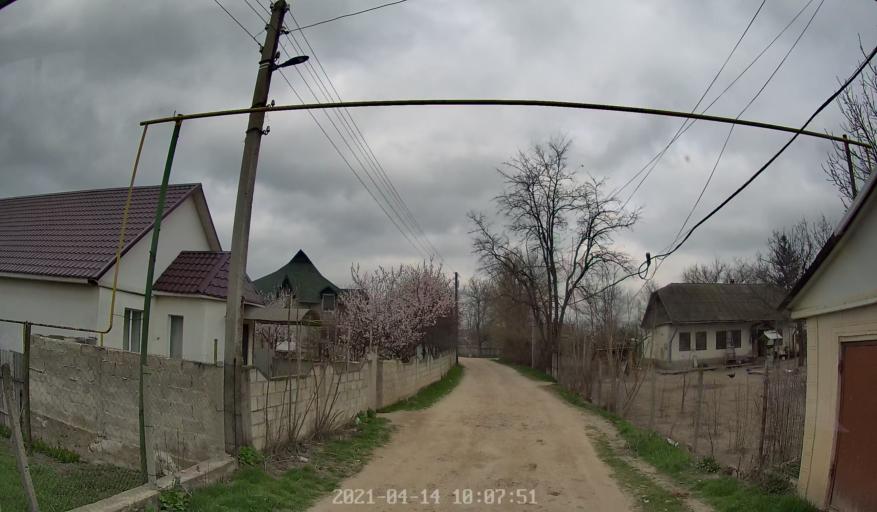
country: MD
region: Criuleni
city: Criuleni
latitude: 47.1445
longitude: 29.1292
